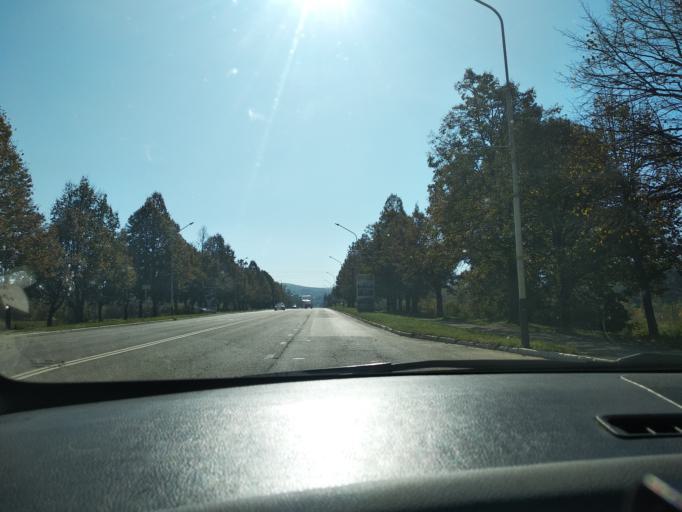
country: RU
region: Krasnodarskiy
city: Goryachiy Klyuch
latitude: 44.6427
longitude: 39.1312
